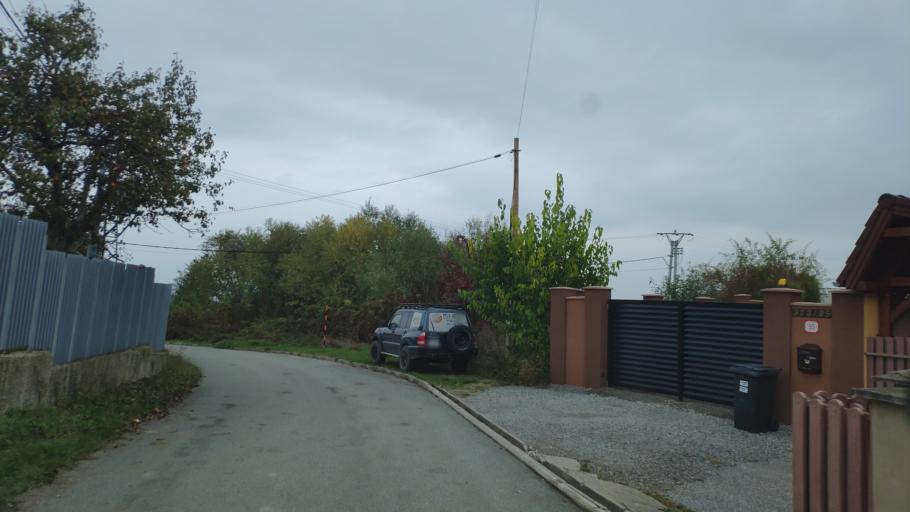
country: SK
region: Kosicky
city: Kosice
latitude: 48.6344
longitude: 21.3934
